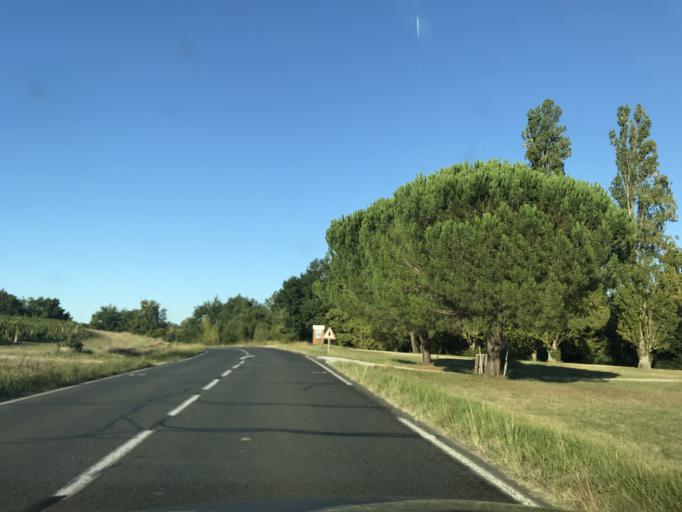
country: FR
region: Aquitaine
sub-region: Departement de la Gironde
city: Sauveterre-de-Guyenne
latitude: 44.6565
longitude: -0.1010
